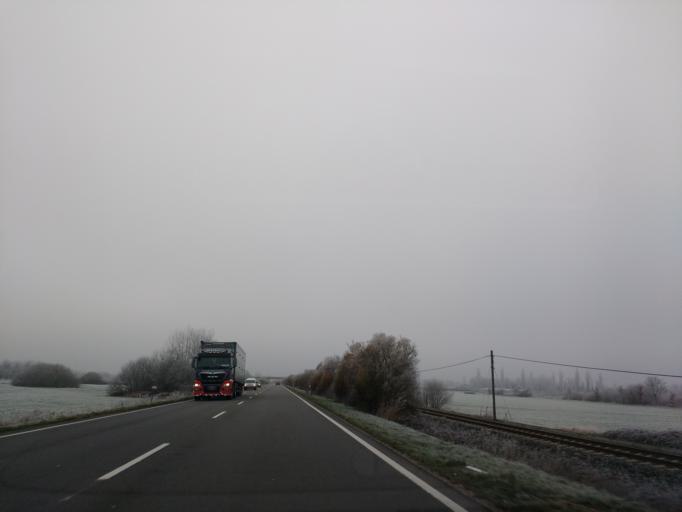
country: DE
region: Baden-Wuerttemberg
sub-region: Freiburg Region
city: Haslach
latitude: 48.5379
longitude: 8.0428
